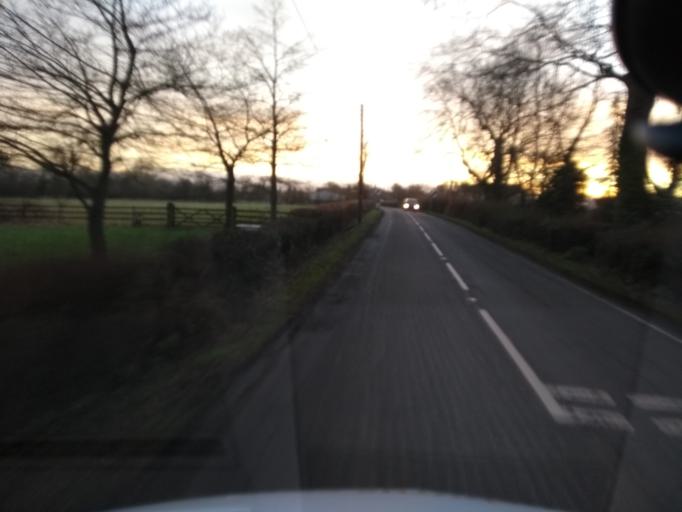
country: GB
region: England
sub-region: Somerset
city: Wedmore
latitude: 51.2267
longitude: -2.8843
